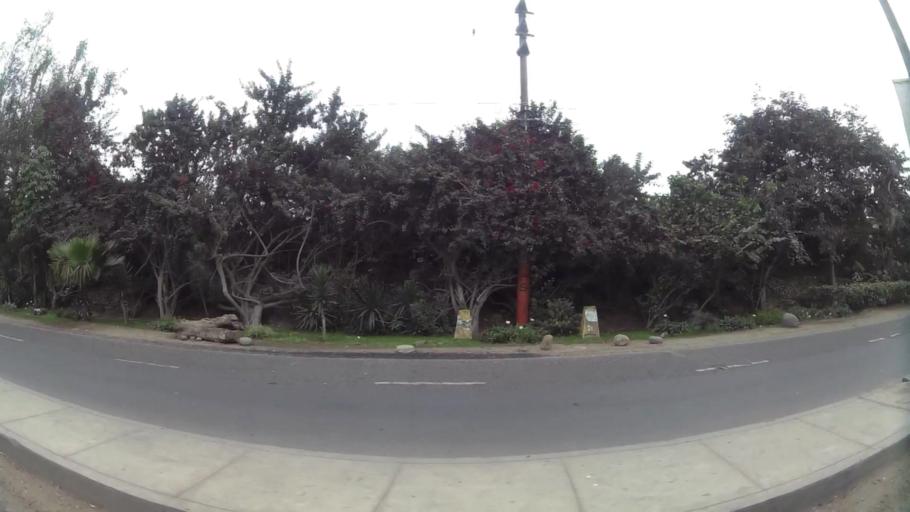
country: PE
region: Lima
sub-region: Lima
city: Independencia
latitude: -11.9382
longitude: -77.0850
